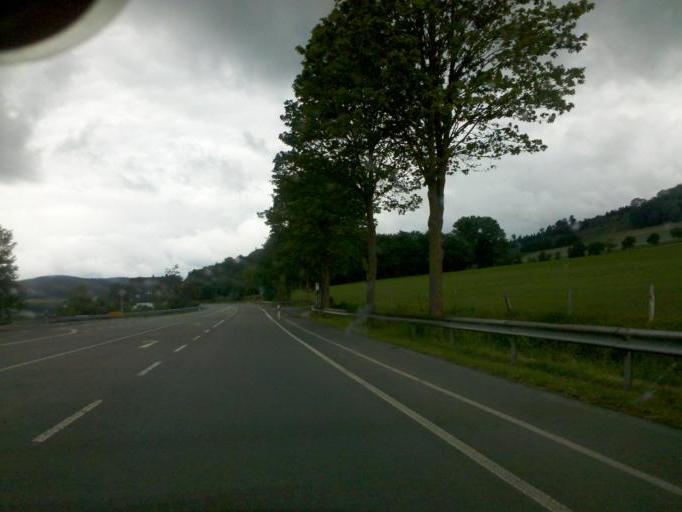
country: DE
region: North Rhine-Westphalia
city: Eslohe
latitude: 51.2582
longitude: 8.2272
